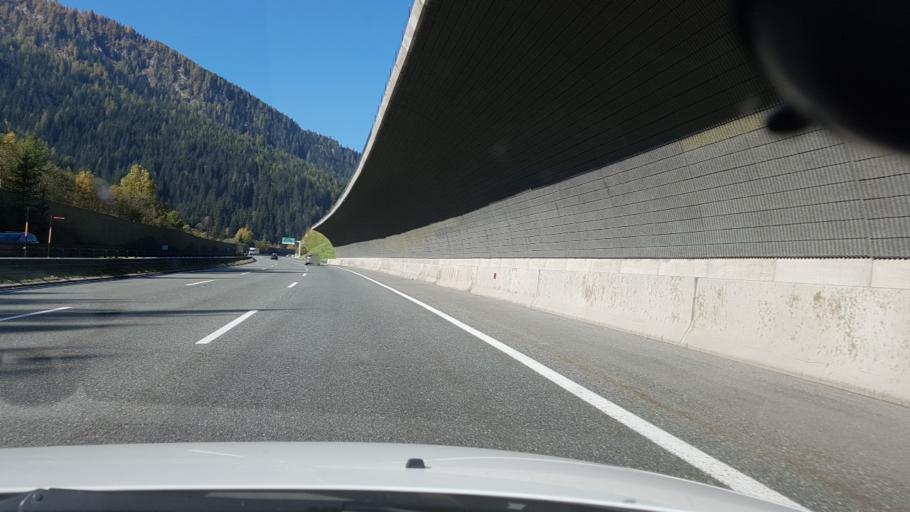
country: AT
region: Salzburg
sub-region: Politischer Bezirk Tamsweg
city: Zederhaus
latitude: 47.1719
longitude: 13.4564
